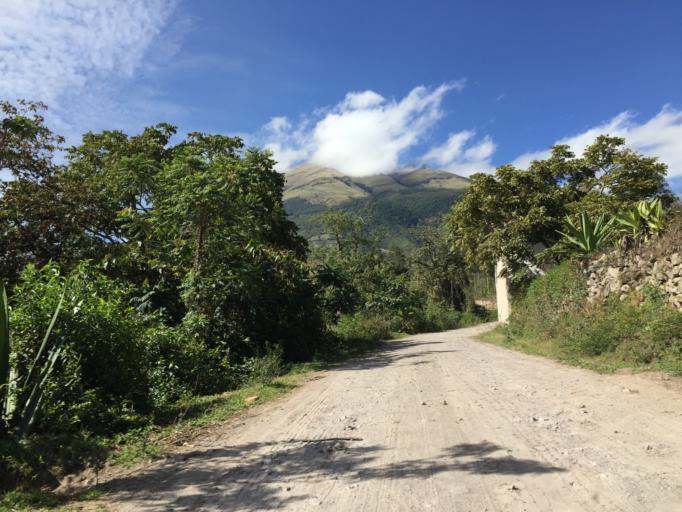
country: EC
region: Imbabura
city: Ibarra
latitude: 0.3105
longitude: -78.1495
